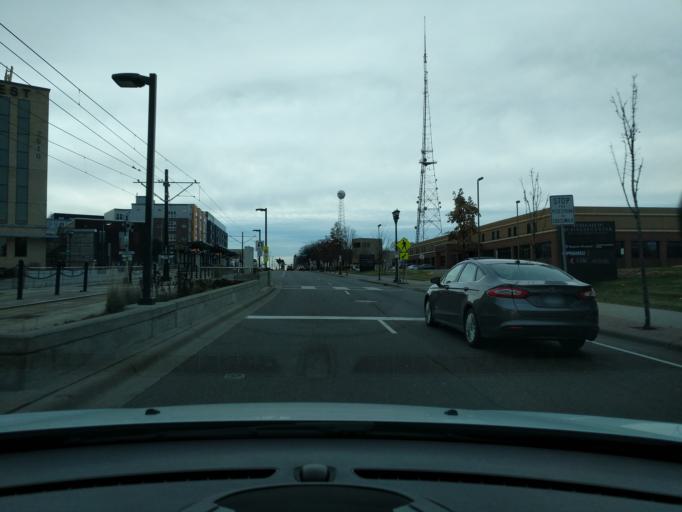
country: US
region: Minnesota
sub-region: Ramsey County
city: Lauderdale
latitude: 44.9668
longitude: -93.2045
